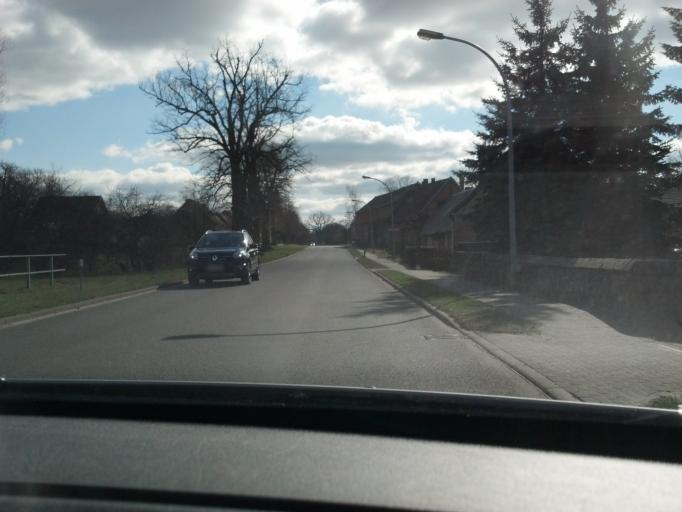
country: DE
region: Brandenburg
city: Gerdshagen
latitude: 53.2914
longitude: 12.1732
